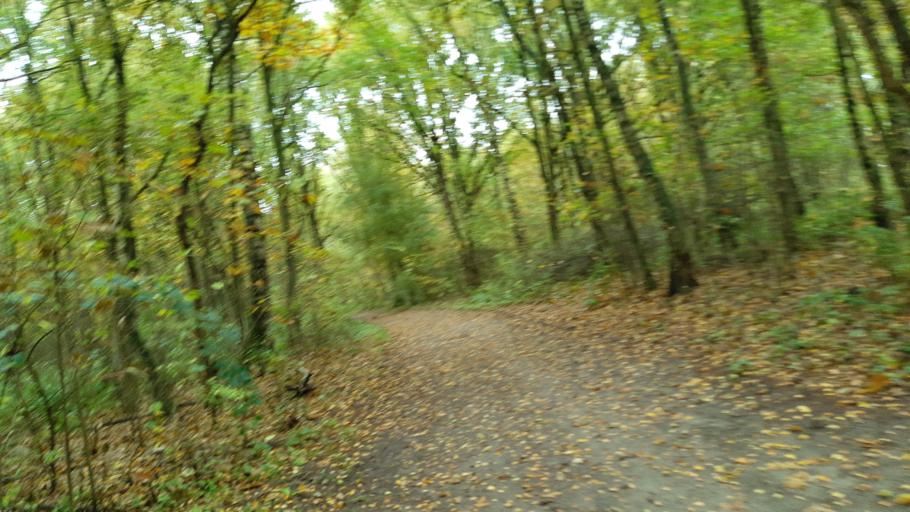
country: NL
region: Friesland
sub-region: Gemeente Lemsterland
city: Echtenerbrug
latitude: 52.7767
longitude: 5.8302
